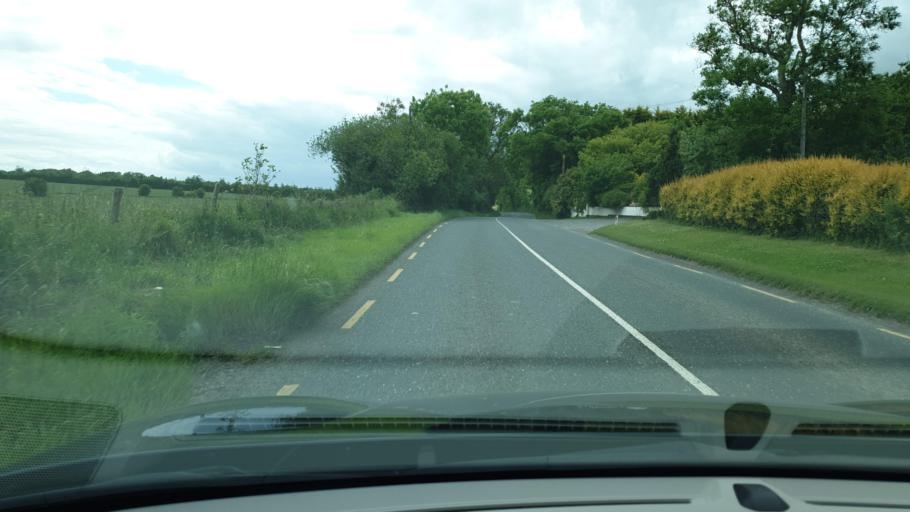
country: IE
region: Leinster
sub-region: An Mhi
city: Ashbourne
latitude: 53.4970
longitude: -6.4083
